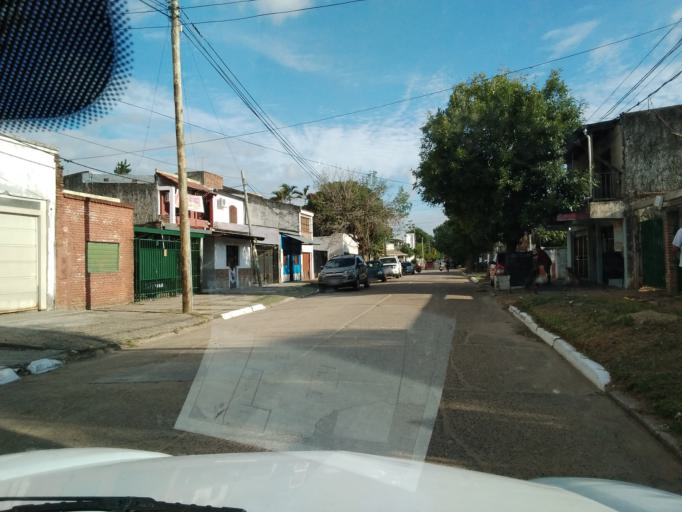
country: AR
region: Corrientes
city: Corrientes
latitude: -27.4610
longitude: -58.8192
